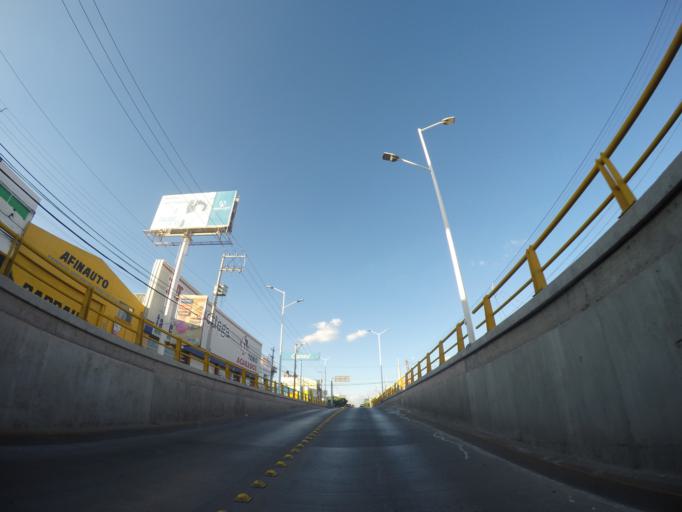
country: MX
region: San Luis Potosi
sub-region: San Luis Potosi
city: San Luis Potosi
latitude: 22.1710
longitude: -101.0014
